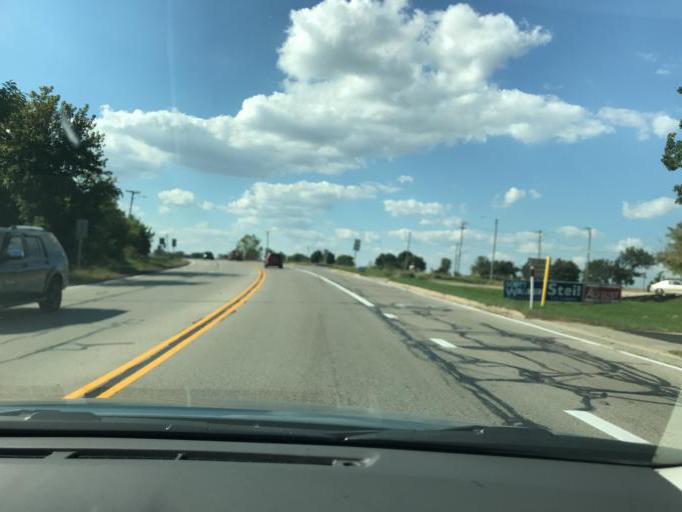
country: US
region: Wisconsin
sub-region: Walworth County
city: Delavan
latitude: 42.6271
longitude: -88.5893
